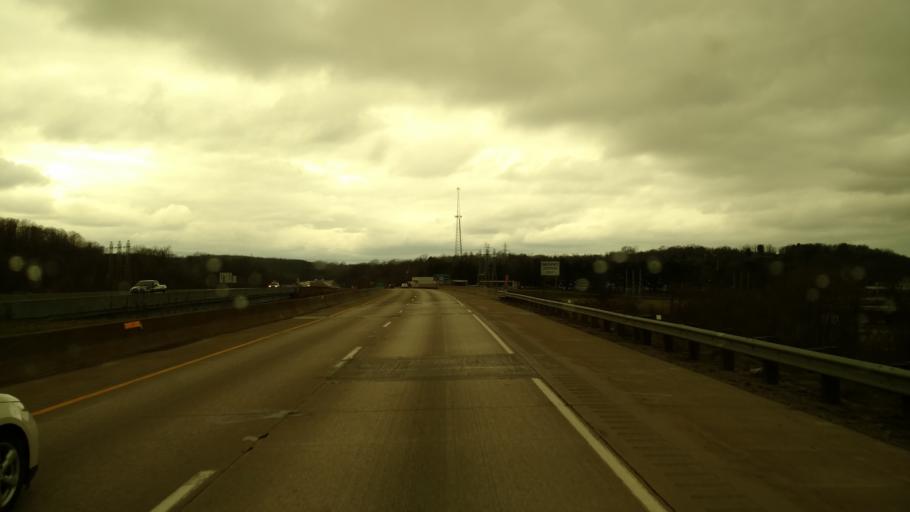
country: US
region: Ohio
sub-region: Muskingum County
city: Zanesville
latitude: 39.9495
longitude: -82.0265
